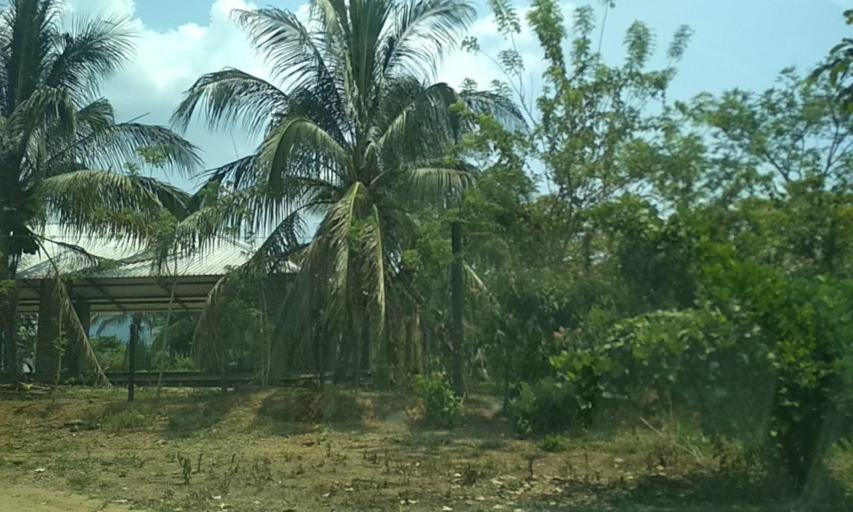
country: MX
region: Chiapas
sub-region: Tecpatan
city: Raudales Malpaso
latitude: 17.3470
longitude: -93.9657
